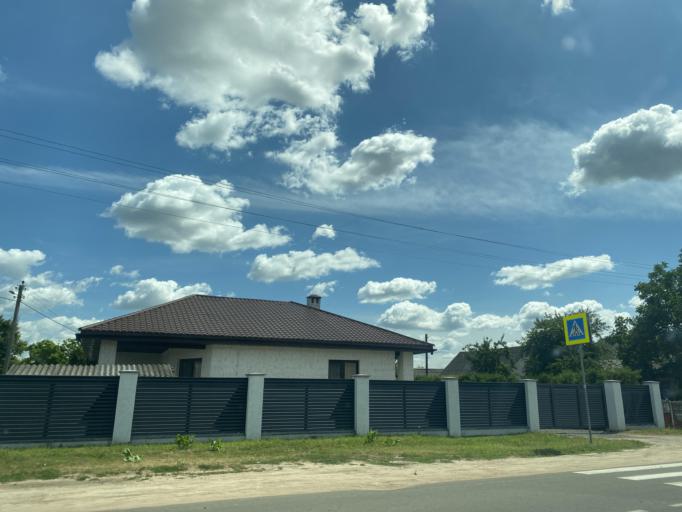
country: BY
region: Brest
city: Ivanava
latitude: 52.1473
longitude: 25.5463
